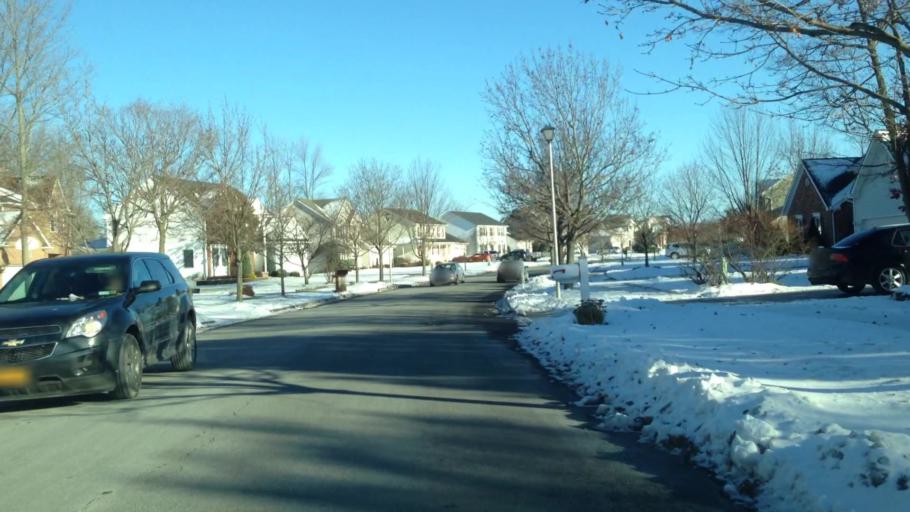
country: US
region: New York
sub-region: Erie County
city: Depew
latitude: 42.8673
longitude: -78.6878
